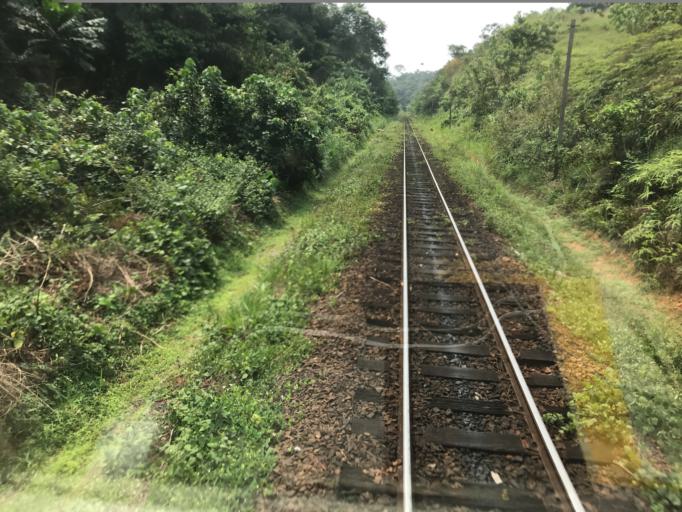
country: CM
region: Centre
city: Eseka
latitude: 3.5779
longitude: 10.8903
